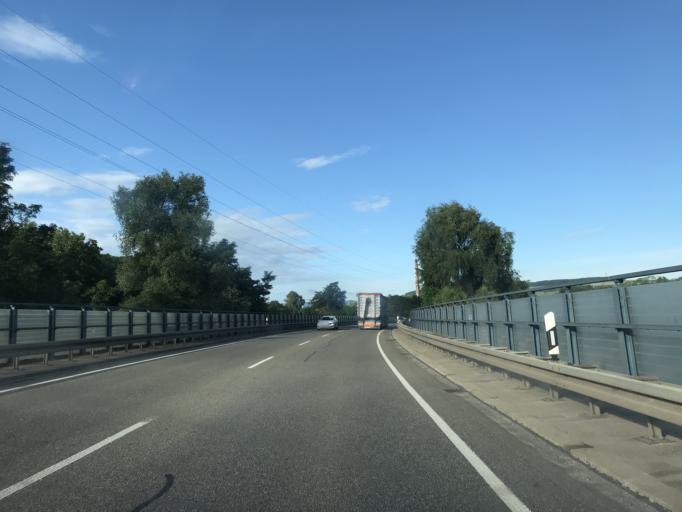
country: DE
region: Baden-Wuerttemberg
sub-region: Freiburg Region
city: Loerrach
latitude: 47.6369
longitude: 7.6894
